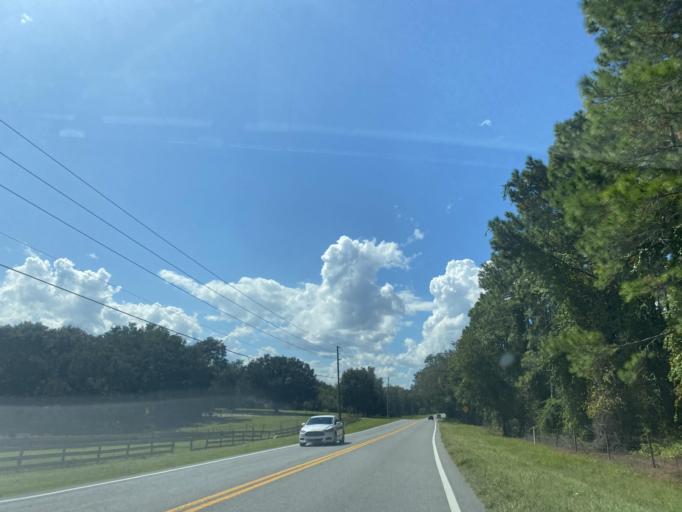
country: US
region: Florida
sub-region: Lake County
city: Lady Lake
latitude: 28.9795
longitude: -81.8657
